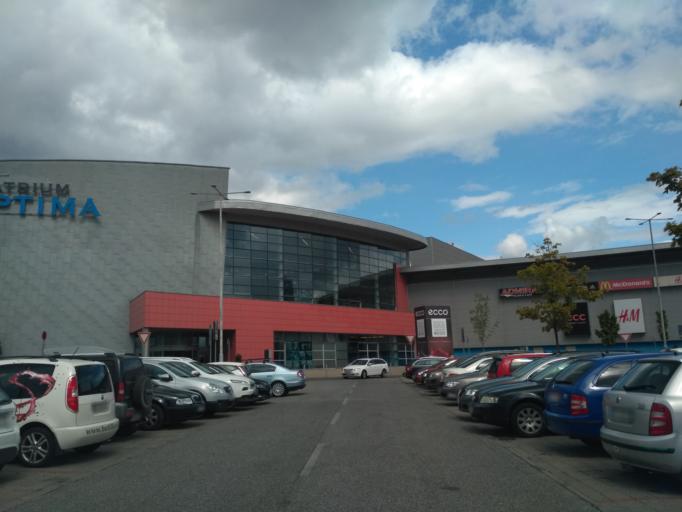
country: SK
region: Kosicky
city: Kosice
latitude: 48.6938
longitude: 21.2391
